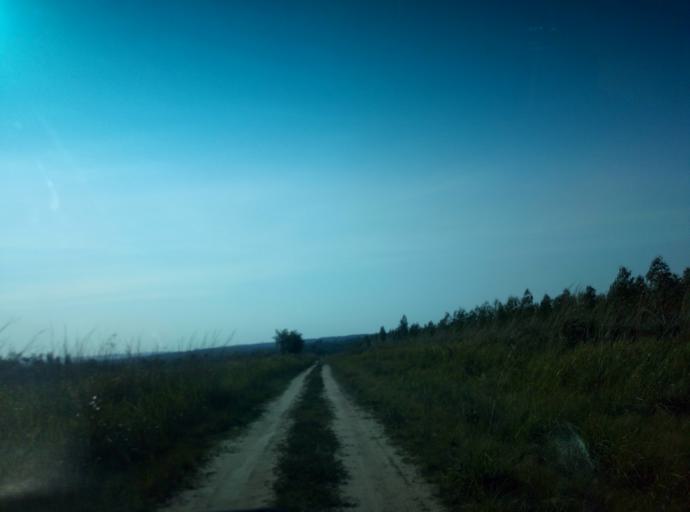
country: PY
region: Caaguazu
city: Doctor Cecilio Baez
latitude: -25.1910
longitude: -56.1963
